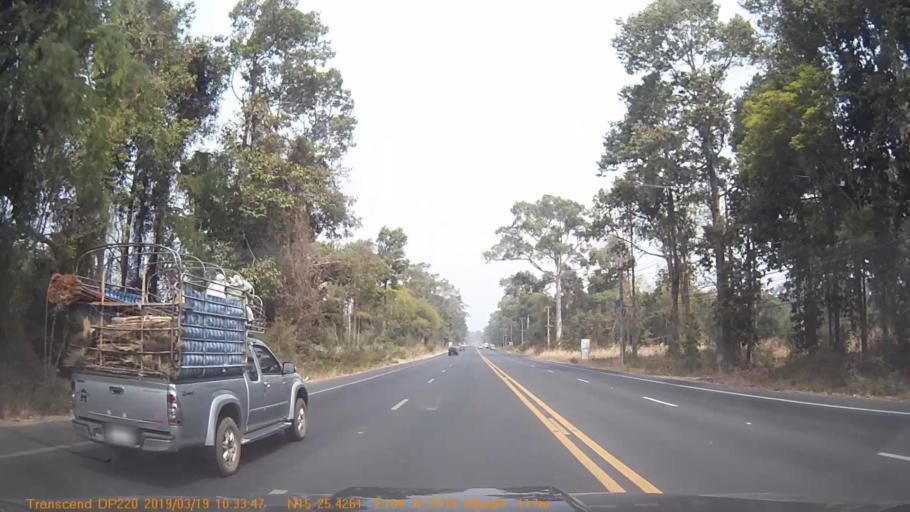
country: TH
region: Changwat Ubon Ratchathani
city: Khueang Nai
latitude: 15.4241
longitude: 104.5374
